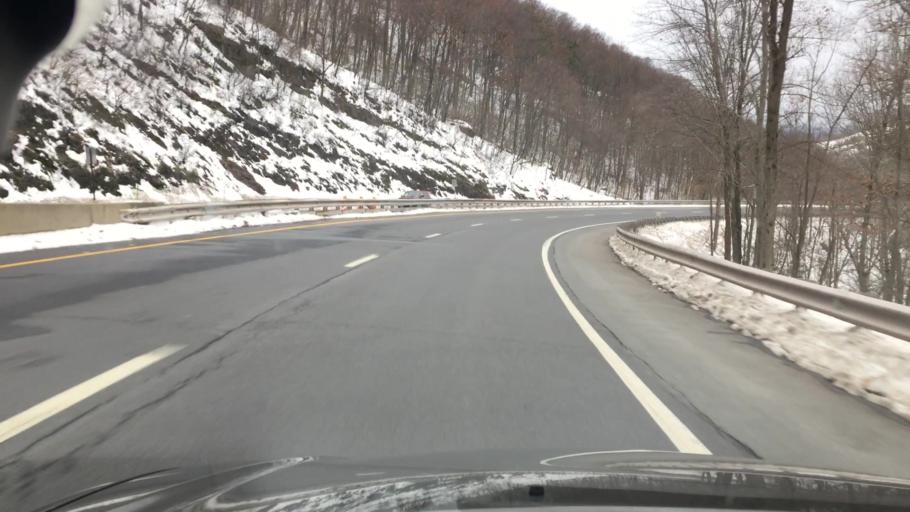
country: US
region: Pennsylvania
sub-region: Luzerne County
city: Mountain Top
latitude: 41.1819
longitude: -75.8897
